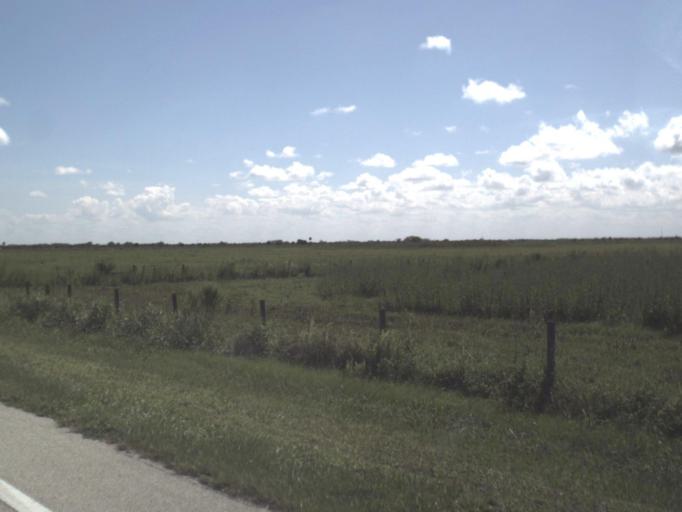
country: US
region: Florida
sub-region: Glades County
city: Moore Haven
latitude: 26.8123
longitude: -81.2232
